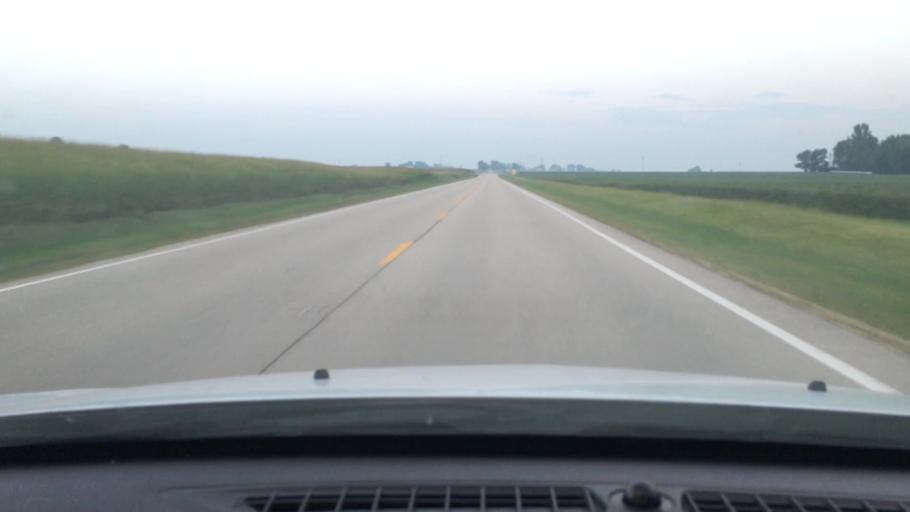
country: US
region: Illinois
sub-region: Ogle County
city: Rochelle
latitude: 41.8514
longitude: -89.0733
